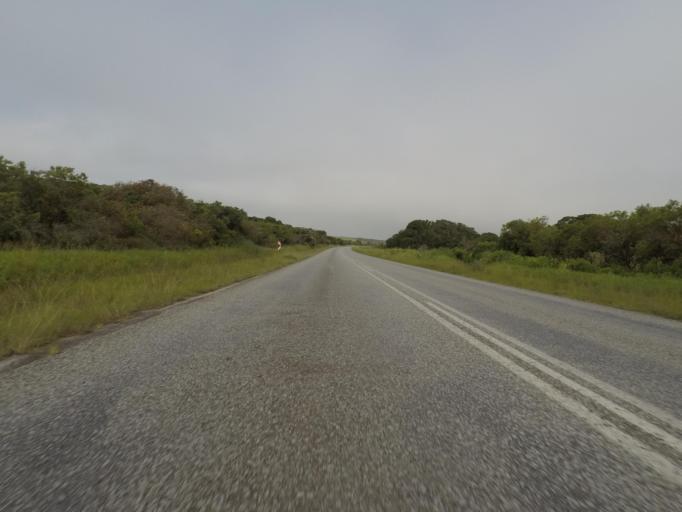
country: ZA
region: Eastern Cape
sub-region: Cacadu District Municipality
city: Port Alfred
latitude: -33.6067
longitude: 26.8238
